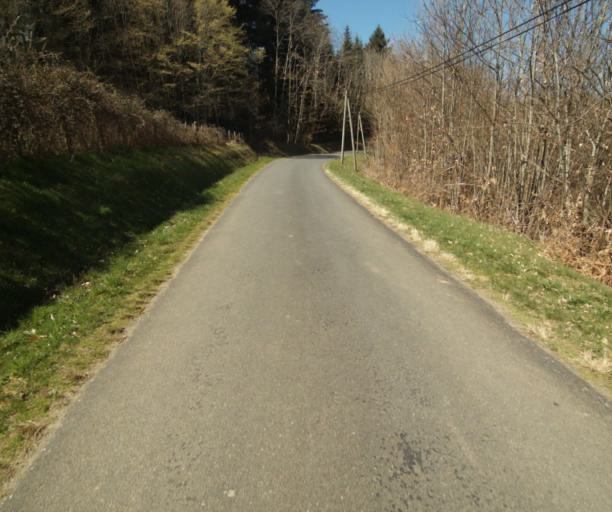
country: FR
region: Limousin
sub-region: Departement de la Correze
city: Saint-Clement
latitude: 45.3313
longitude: 1.6961
